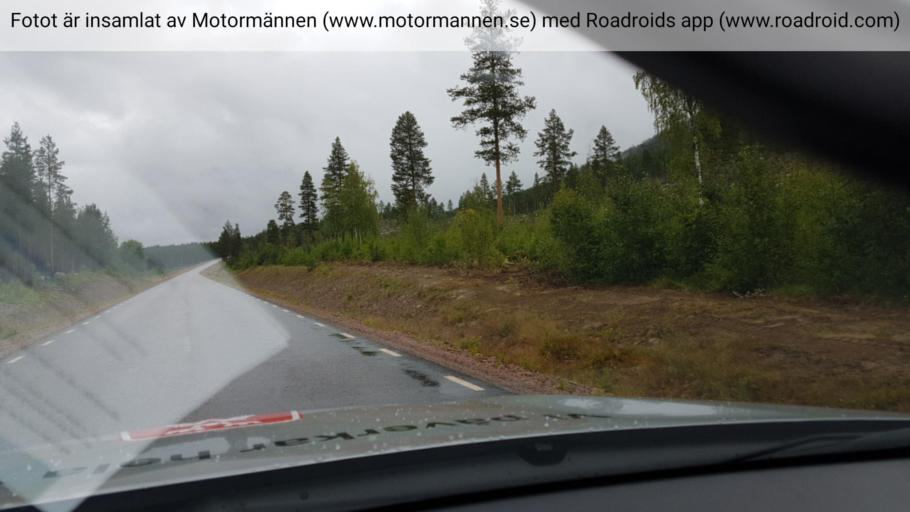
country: SE
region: Norrbotten
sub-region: Gallivare Kommun
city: Gaellivare
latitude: 66.6682
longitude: 20.3713
